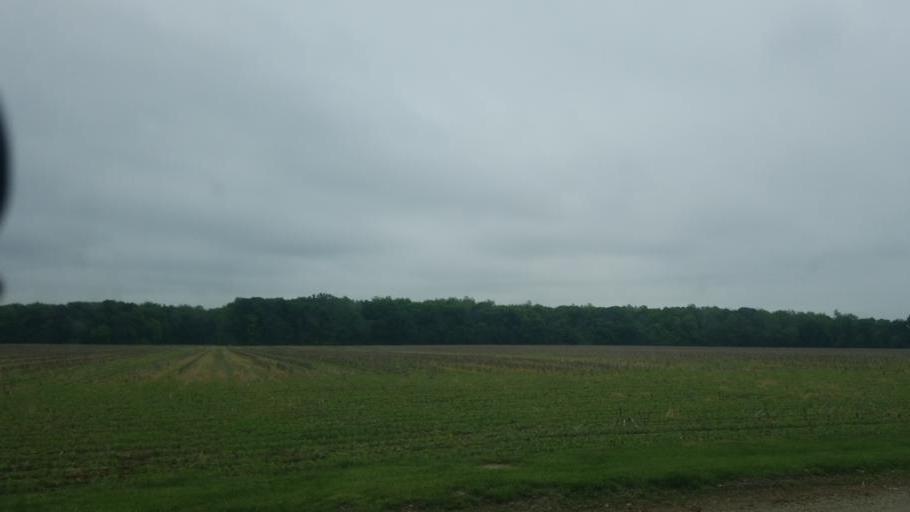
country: US
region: Indiana
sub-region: Elkhart County
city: Nappanee
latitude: 41.4681
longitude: -86.0402
